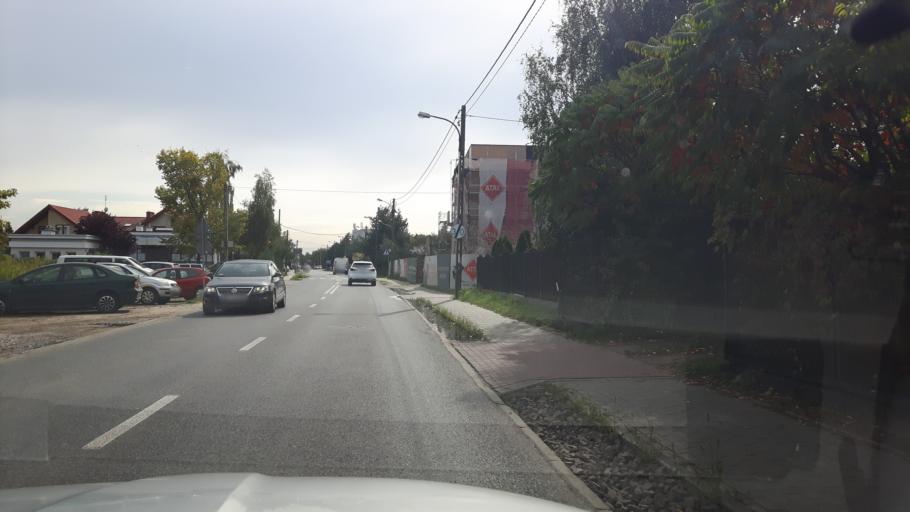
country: PL
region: Masovian Voivodeship
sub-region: Warszawa
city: Targowek
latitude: 52.3203
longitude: 21.0495
